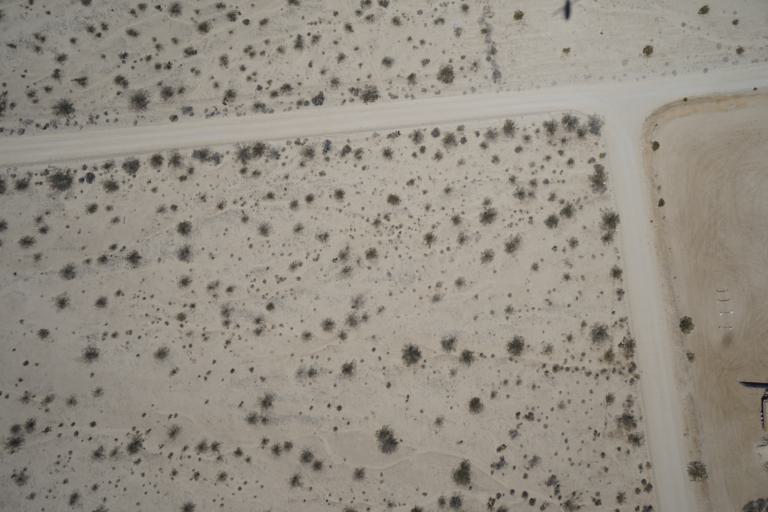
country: US
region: California
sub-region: San Bernardino County
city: Twentynine Palms
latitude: 34.1300
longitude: -116.0274
